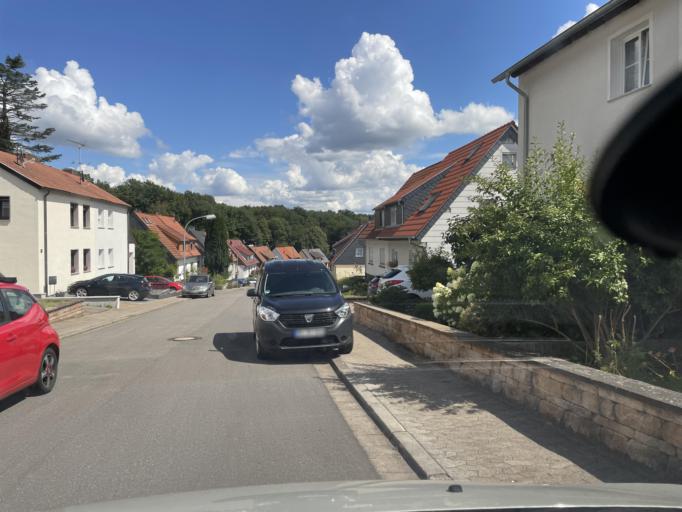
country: DE
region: Saarland
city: Sulzbach
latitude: 49.2731
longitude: 7.0544
